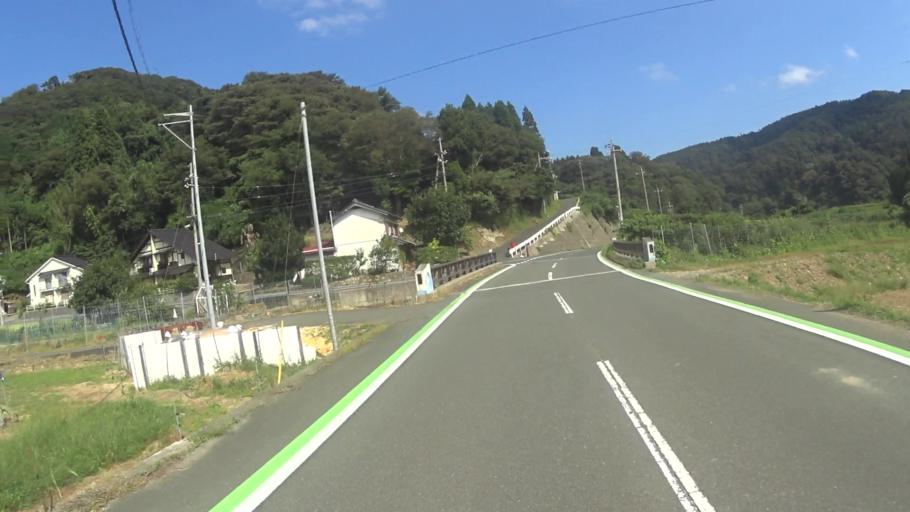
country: JP
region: Kyoto
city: Miyazu
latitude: 35.7301
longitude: 135.2594
